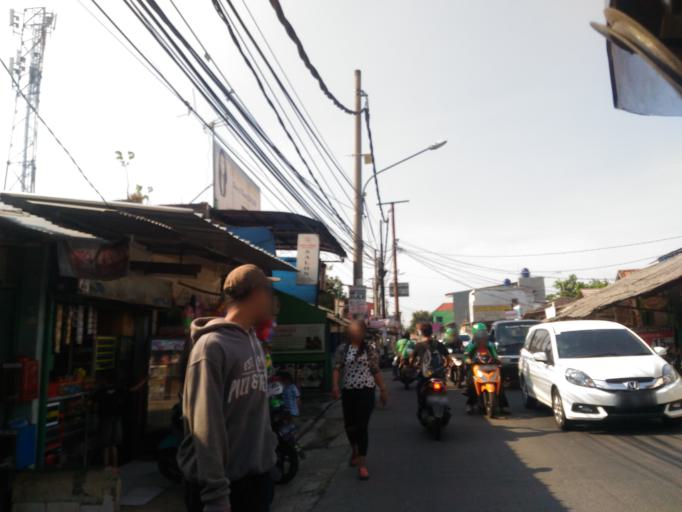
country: ID
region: West Java
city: Depok
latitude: -6.3548
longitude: 106.8426
